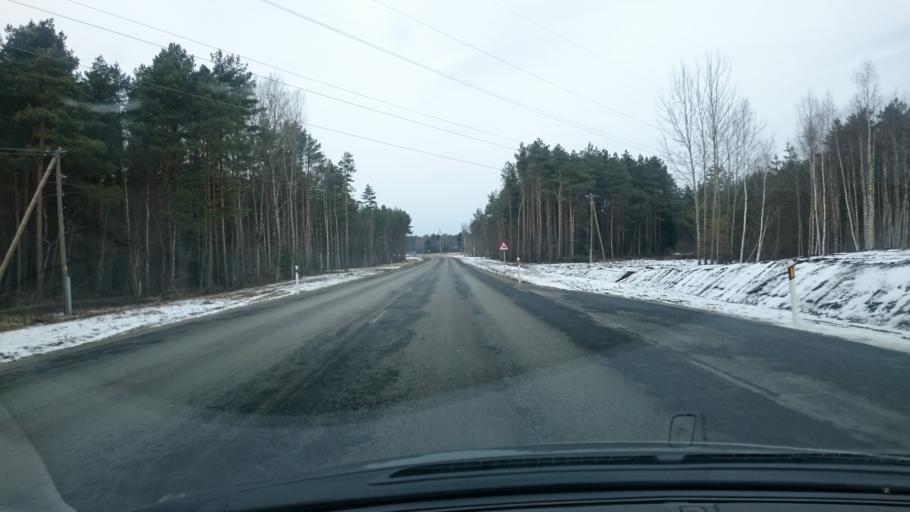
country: EE
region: Harju
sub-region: Saue vald
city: Laagri
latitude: 59.3537
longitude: 24.5999
